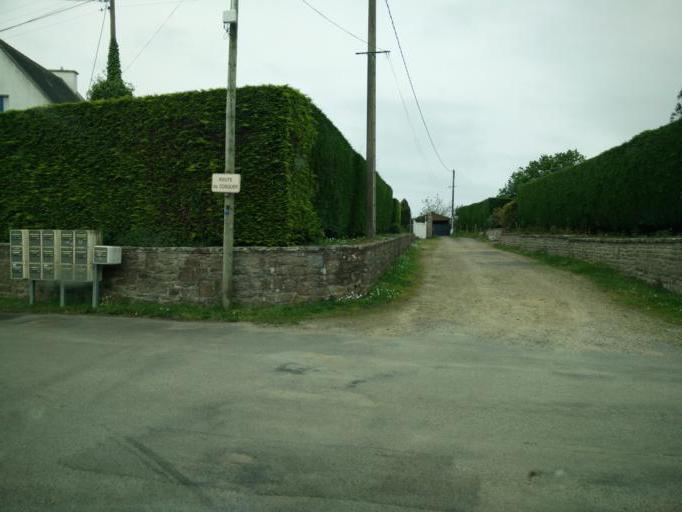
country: FR
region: Brittany
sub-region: Departement du Finistere
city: Tregunc
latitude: 47.8306
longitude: -3.8768
